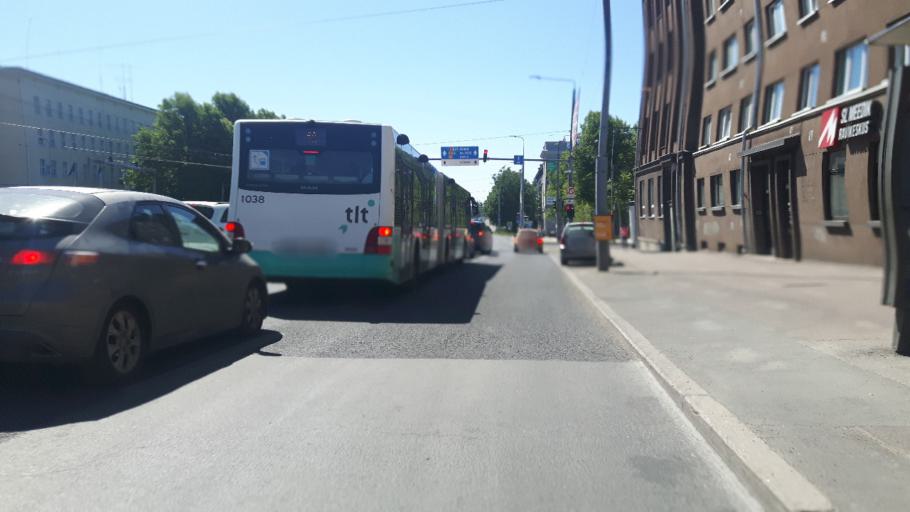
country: EE
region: Harju
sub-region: Tallinna linn
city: Tallinn
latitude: 59.4279
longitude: 24.7423
